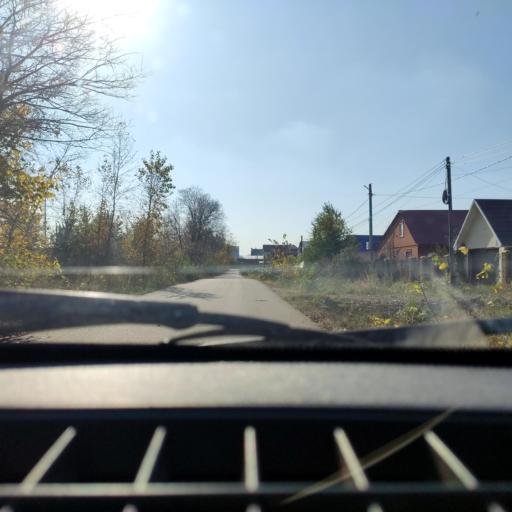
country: RU
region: Bashkortostan
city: Ufa
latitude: 54.6244
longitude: 55.9112
